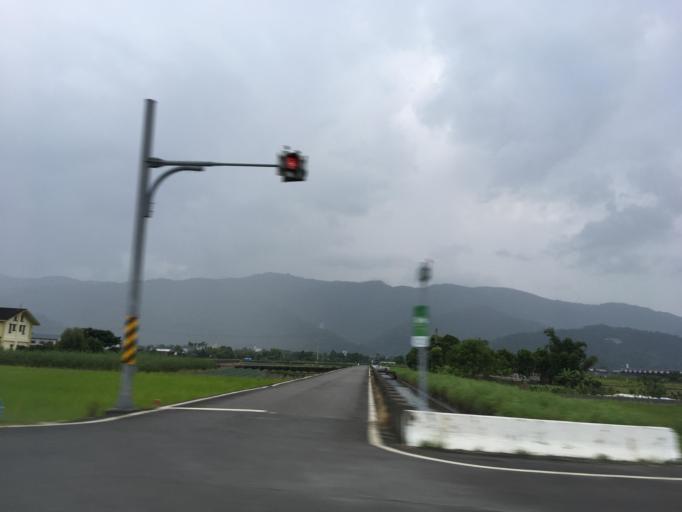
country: TW
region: Taiwan
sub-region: Yilan
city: Yilan
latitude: 24.6771
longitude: 121.6506
